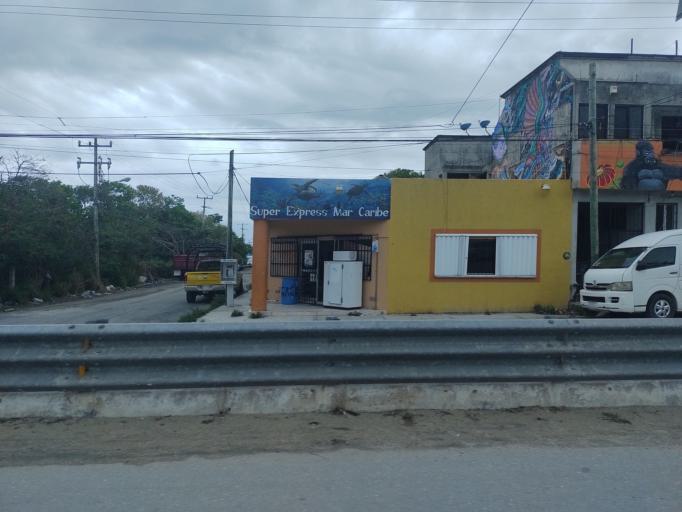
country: MX
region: Quintana Roo
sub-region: Tulum
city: Ciudad Chemuyil
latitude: 20.4000
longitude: -87.3204
